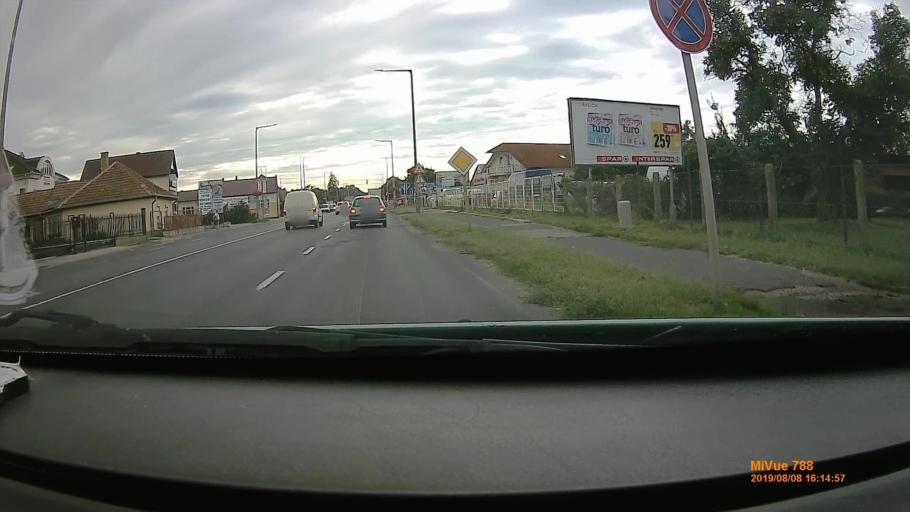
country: HU
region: Szabolcs-Szatmar-Bereg
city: Mateszalka
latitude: 47.9604
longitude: 22.3120
